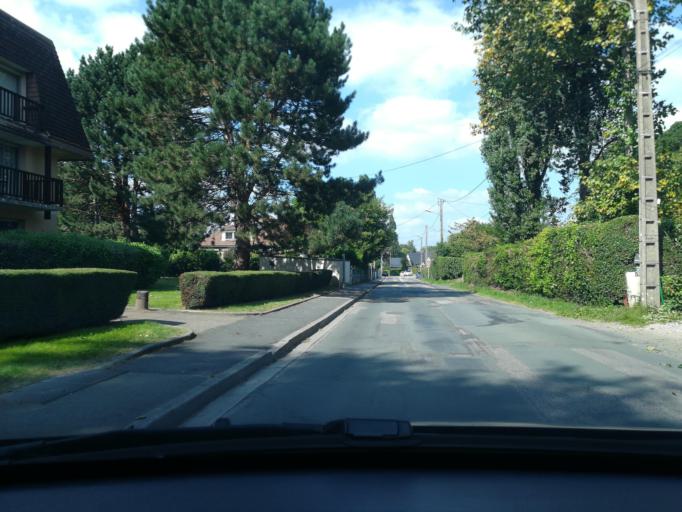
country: FR
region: Haute-Normandie
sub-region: Departement de la Seine-Maritime
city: Bois-Guillaume
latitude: 49.4665
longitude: 1.1261
